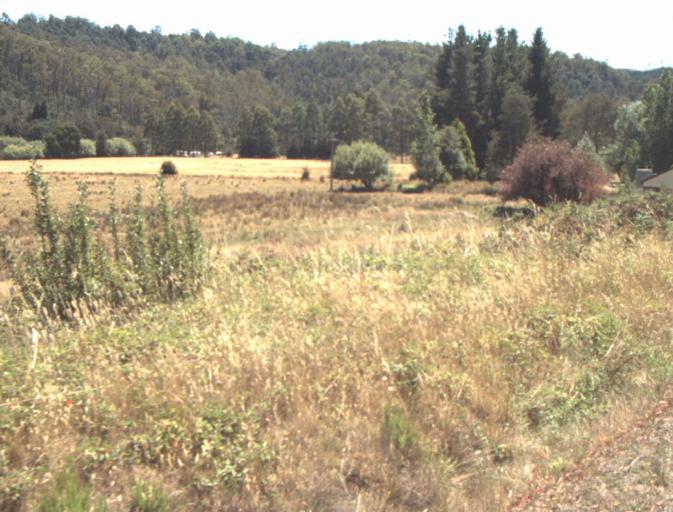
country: AU
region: Tasmania
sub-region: Dorset
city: Scottsdale
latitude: -41.3159
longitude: 147.3669
